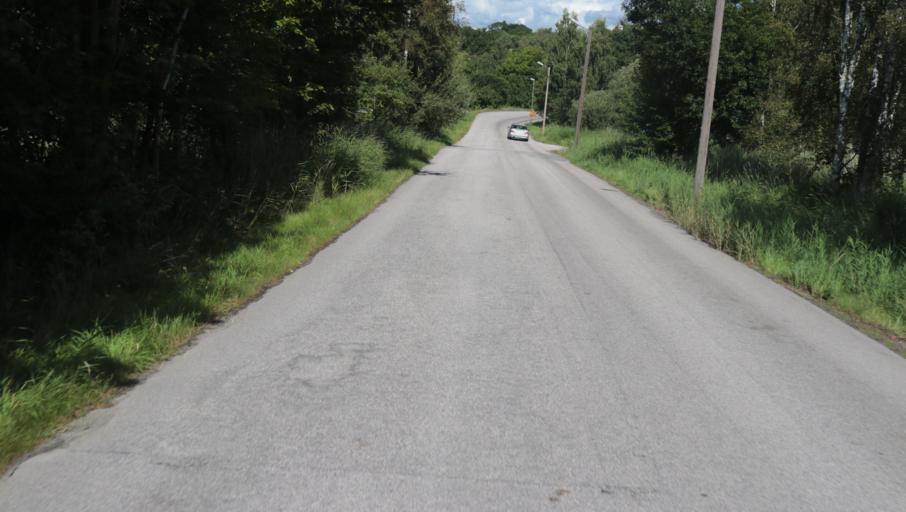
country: SE
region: Blekinge
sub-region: Karlshamns Kommun
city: Karlshamn
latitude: 56.1566
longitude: 14.8520
